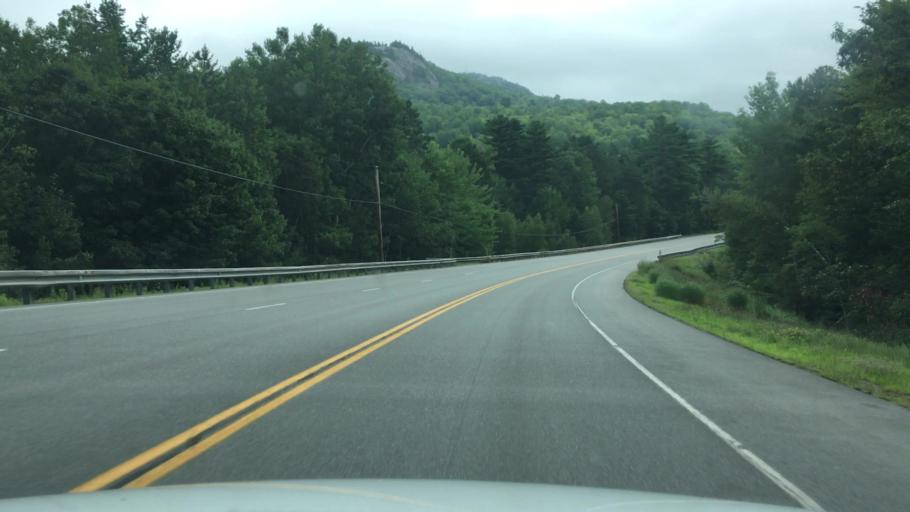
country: US
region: Maine
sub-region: Penobscot County
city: Bradley
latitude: 44.8253
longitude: -68.4895
